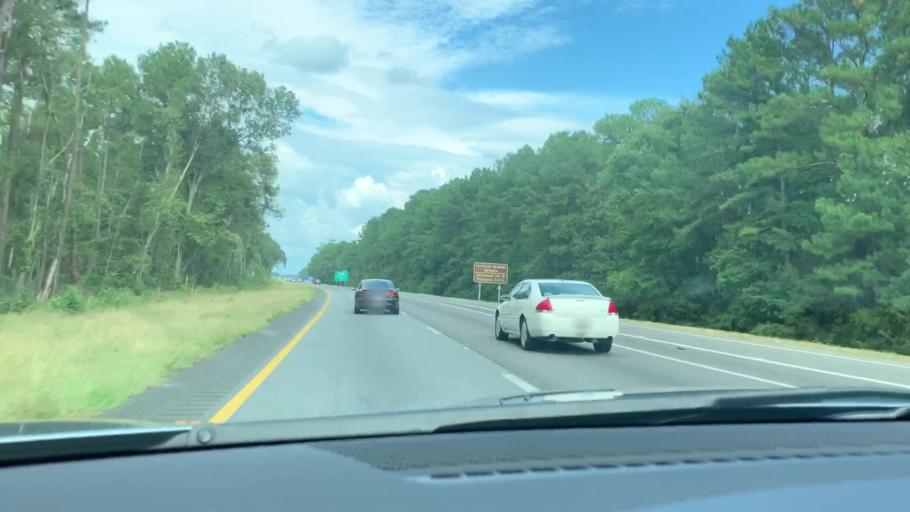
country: US
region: South Carolina
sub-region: Jasper County
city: Hardeeville
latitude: 32.2581
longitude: -81.0971
